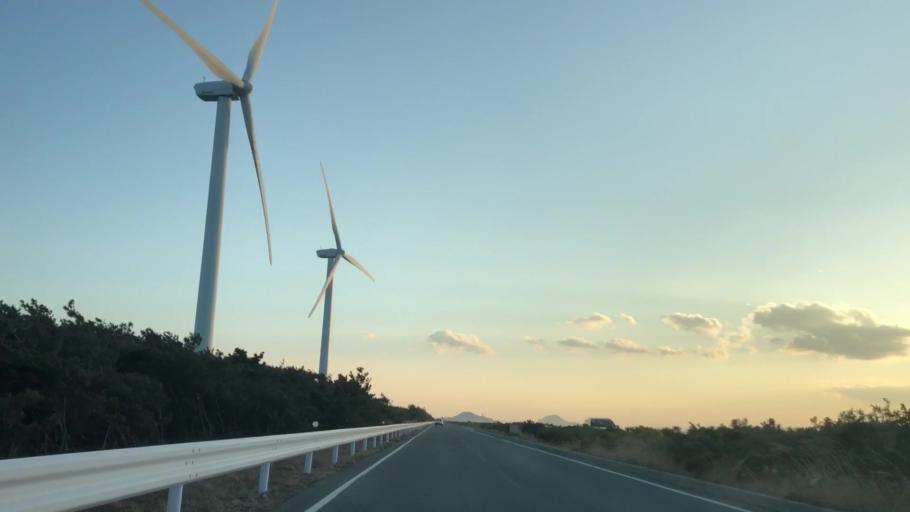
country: JP
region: Aichi
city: Toyohama
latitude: 34.6392
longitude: 137.0529
